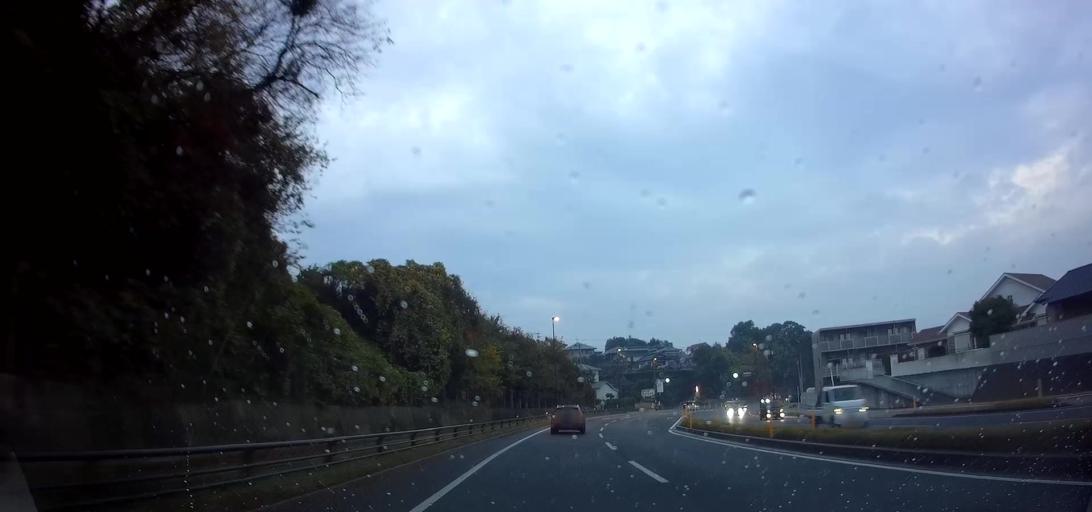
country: JP
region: Nagasaki
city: Omura
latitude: 32.8950
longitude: 129.9640
